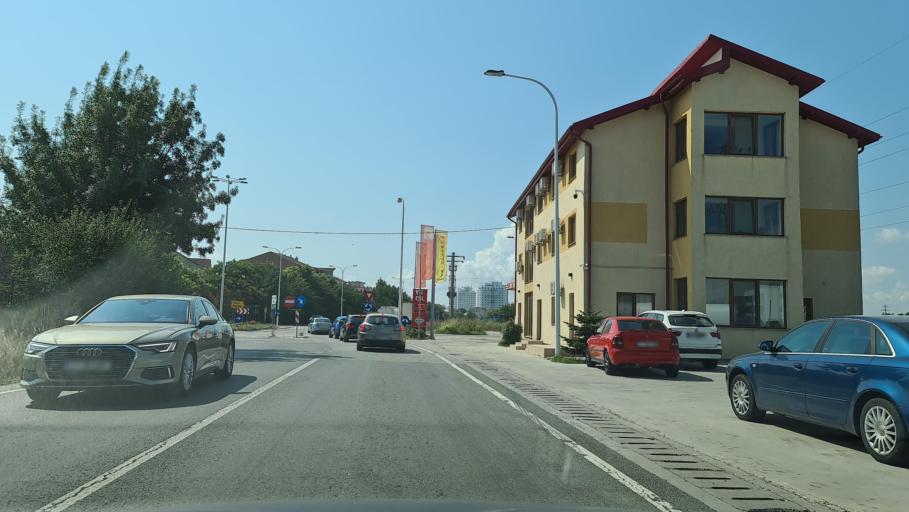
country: RO
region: Constanta
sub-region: Oras Eforie
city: Eforie Nord
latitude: 44.0832
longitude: 28.6396
